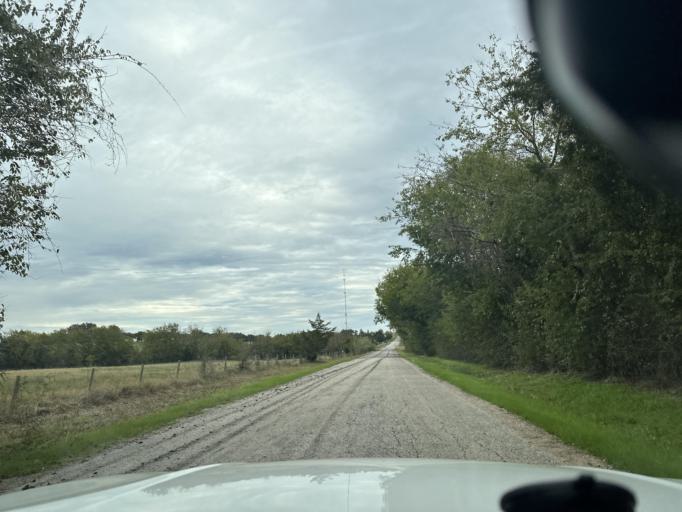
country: US
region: Texas
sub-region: Burleson County
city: Somerville
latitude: 30.1596
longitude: -96.6427
